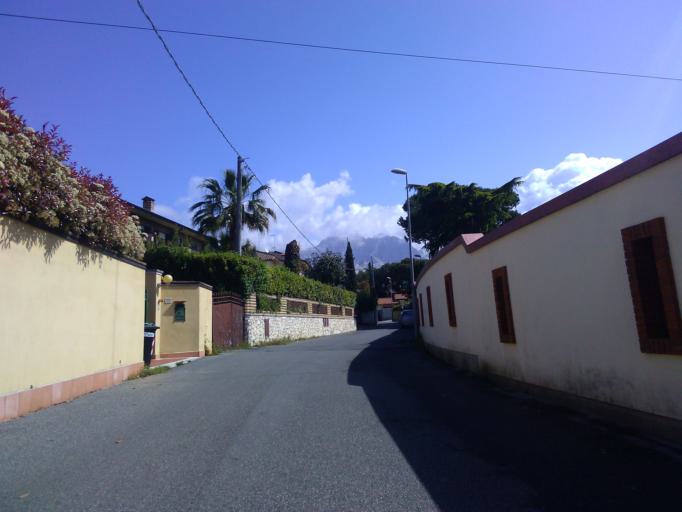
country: IT
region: Tuscany
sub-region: Provincia di Massa-Carrara
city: Carrara
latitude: 44.0612
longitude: 10.0657
